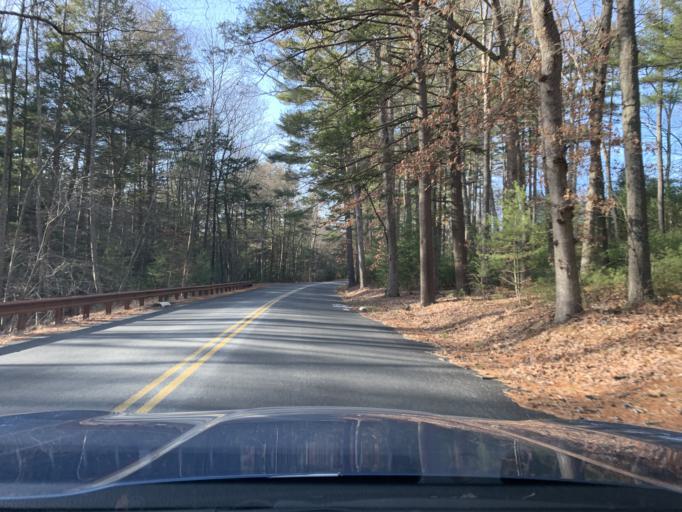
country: US
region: Connecticut
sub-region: Hartford County
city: Weatogue
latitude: 41.8510
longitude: -72.8172
